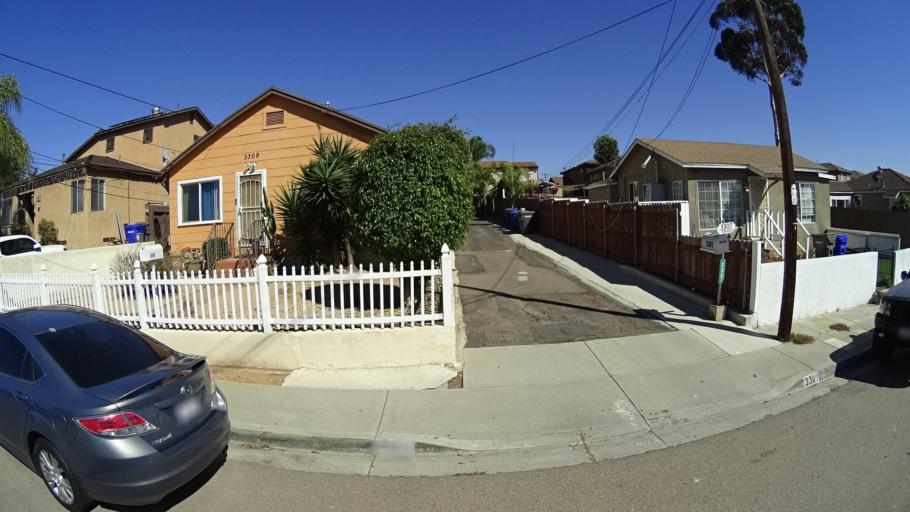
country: US
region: California
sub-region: San Diego County
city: Chula Vista
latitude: 32.6612
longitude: -117.0728
